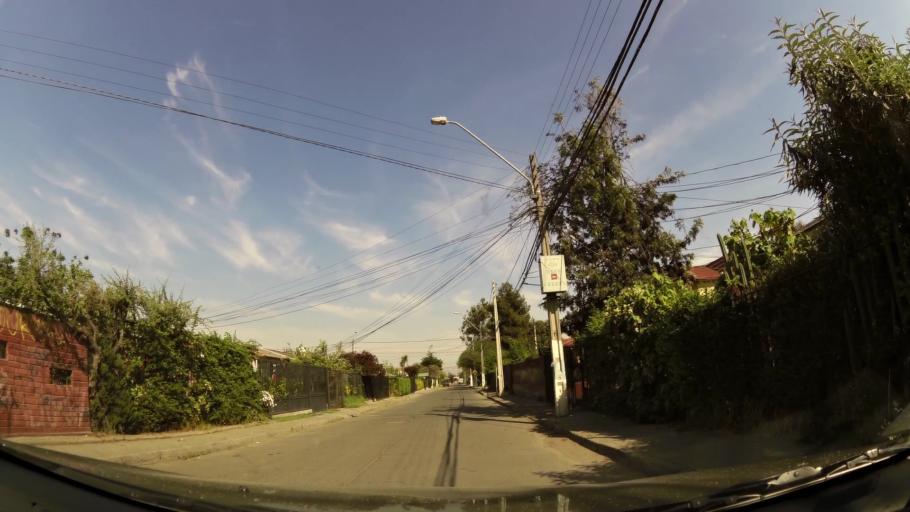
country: CL
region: Santiago Metropolitan
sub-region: Provincia de Cordillera
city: Puente Alto
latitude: -33.5702
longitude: -70.5860
